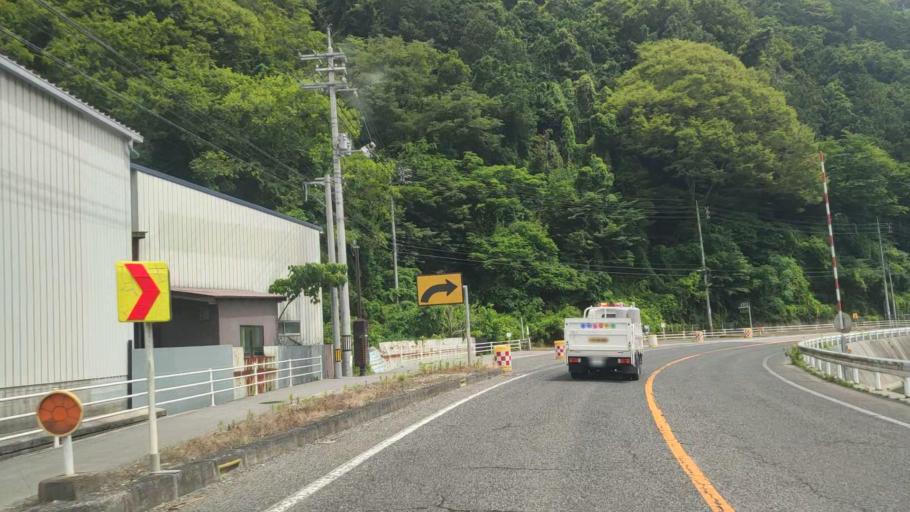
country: JP
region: Okayama
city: Niimi
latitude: 35.0741
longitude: 133.6806
